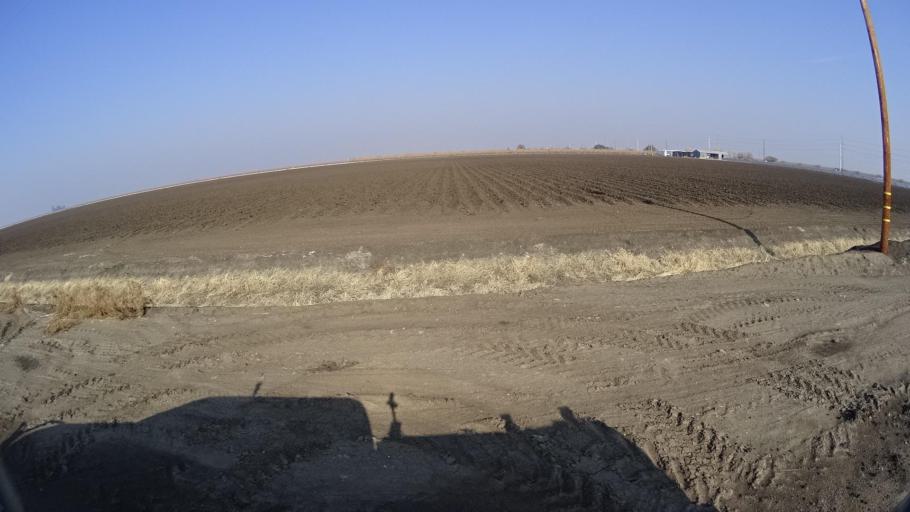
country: US
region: California
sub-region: Kern County
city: Buttonwillow
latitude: 35.3545
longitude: -119.4509
